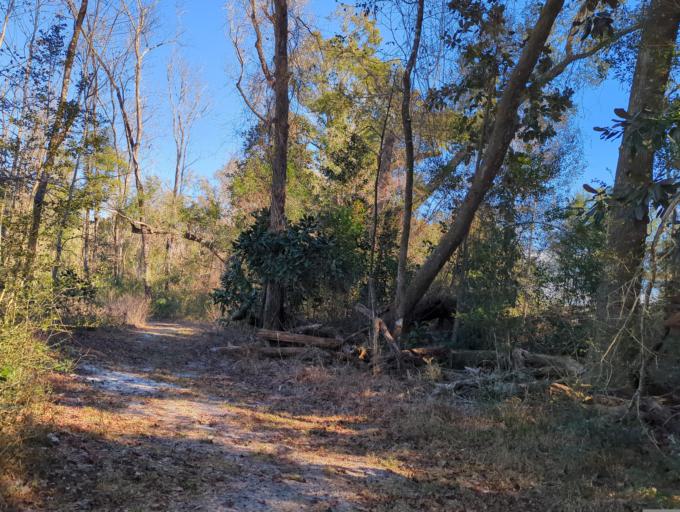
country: US
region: Florida
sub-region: Wakulla County
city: Crawfordville
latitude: 30.1826
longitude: -84.3306
